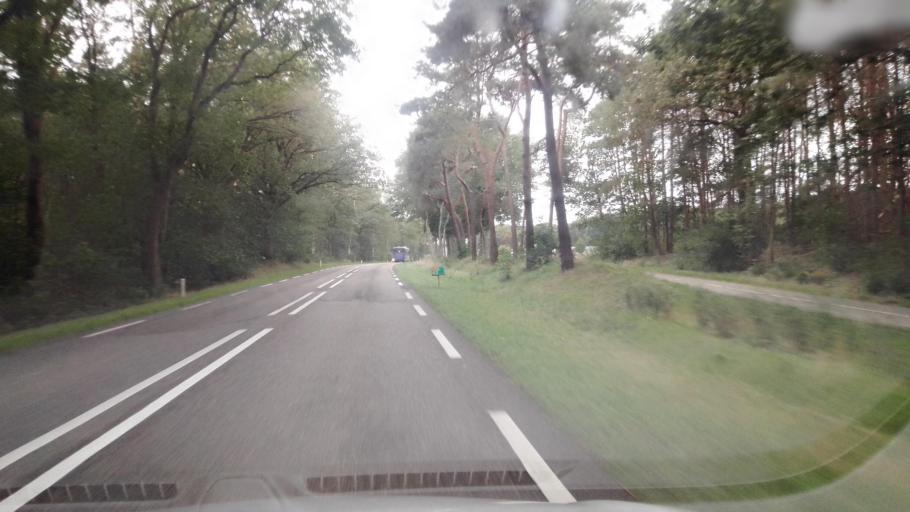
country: NL
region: Limburg
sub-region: Gemeente Peel en Maas
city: Maasbree
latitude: 51.3646
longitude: 6.0879
